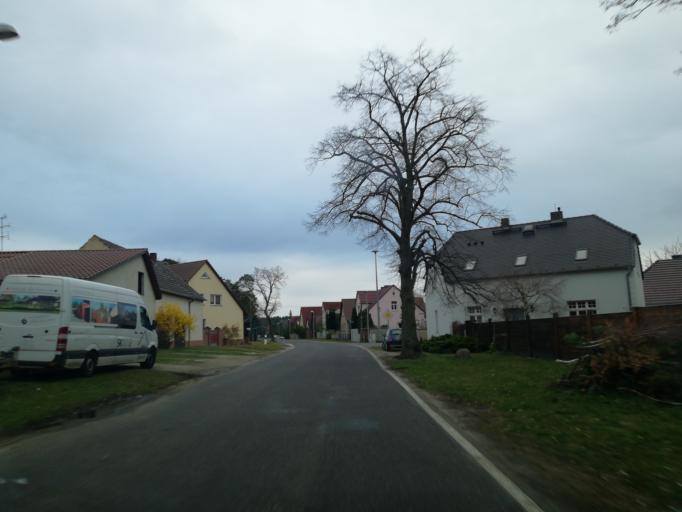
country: DE
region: Brandenburg
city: Vetschau
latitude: 51.7611
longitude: 14.1302
